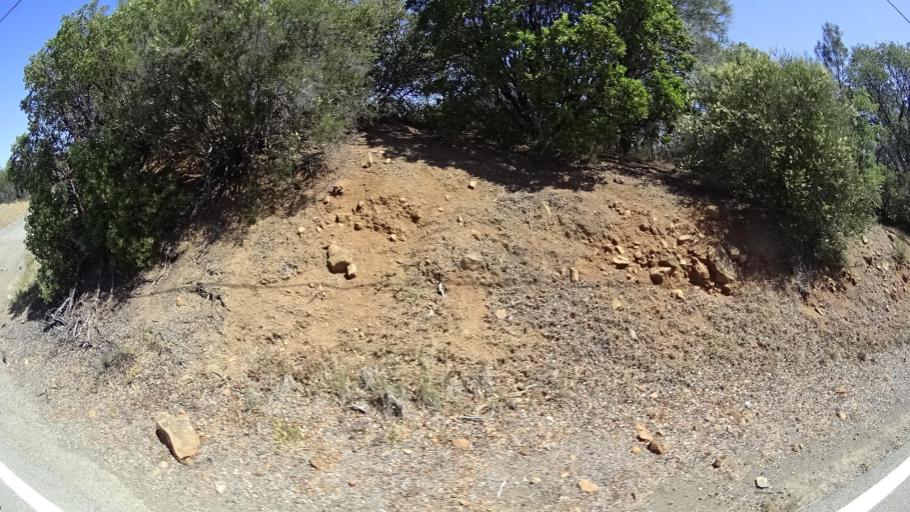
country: US
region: California
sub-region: Lake County
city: Hidden Valley Lake
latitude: 38.8853
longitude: -122.4601
